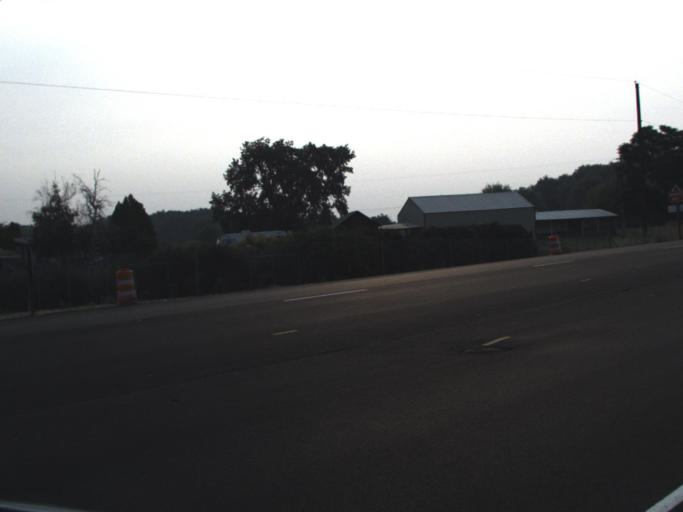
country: US
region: Washington
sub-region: Yakima County
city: Wapato
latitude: 46.4031
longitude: -120.3773
